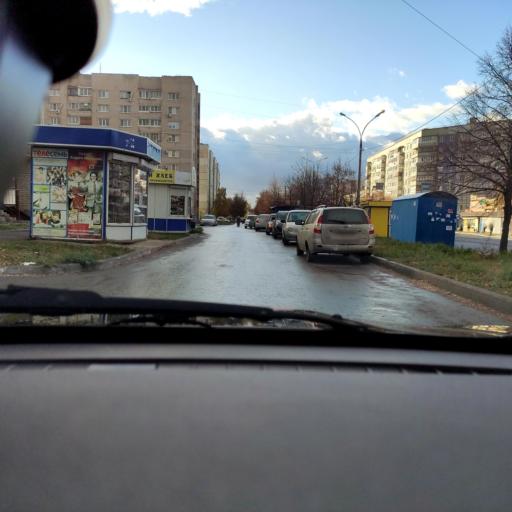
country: RU
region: Samara
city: Tol'yatti
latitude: 53.5390
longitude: 49.4019
